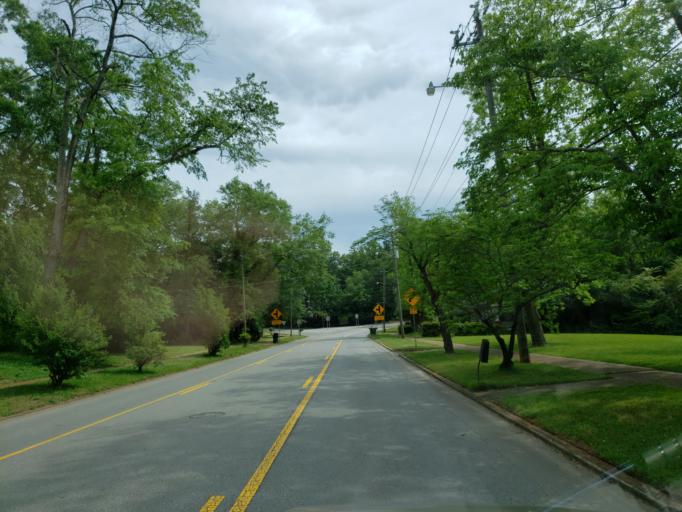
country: US
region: Georgia
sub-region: Monroe County
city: Forsyth
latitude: 33.0307
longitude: -83.9385
